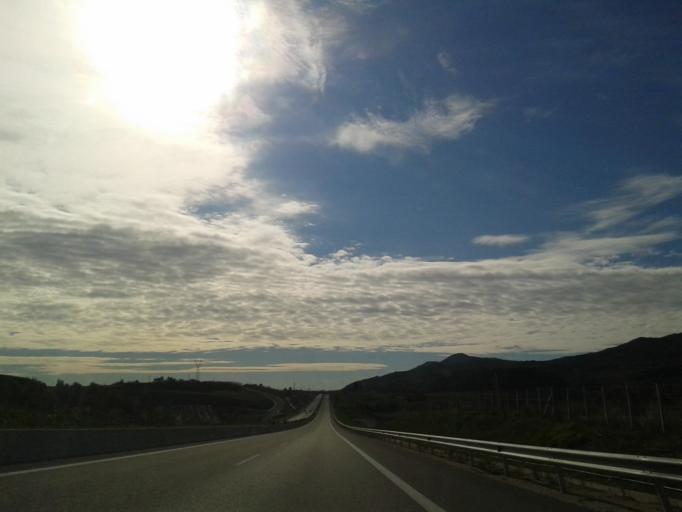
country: GR
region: West Greece
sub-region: Nomos Aitolias kai Akarnanias
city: Fitiai
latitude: 38.7130
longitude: 21.2082
